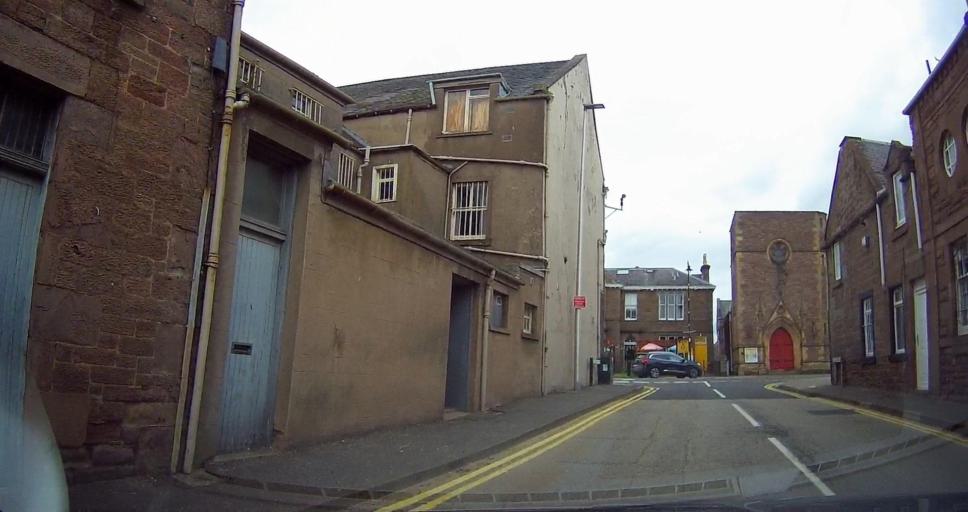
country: GB
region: Scotland
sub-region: Angus
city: Forfar
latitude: 56.6444
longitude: -2.8851
